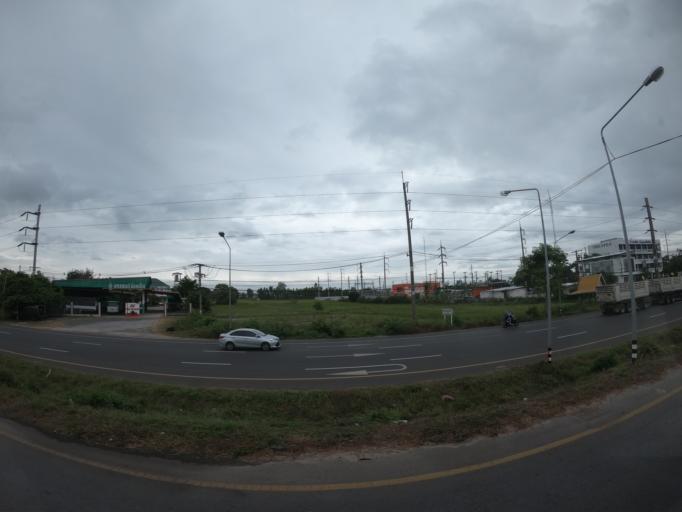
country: TH
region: Roi Et
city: Roi Et
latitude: 16.0452
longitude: 103.6257
